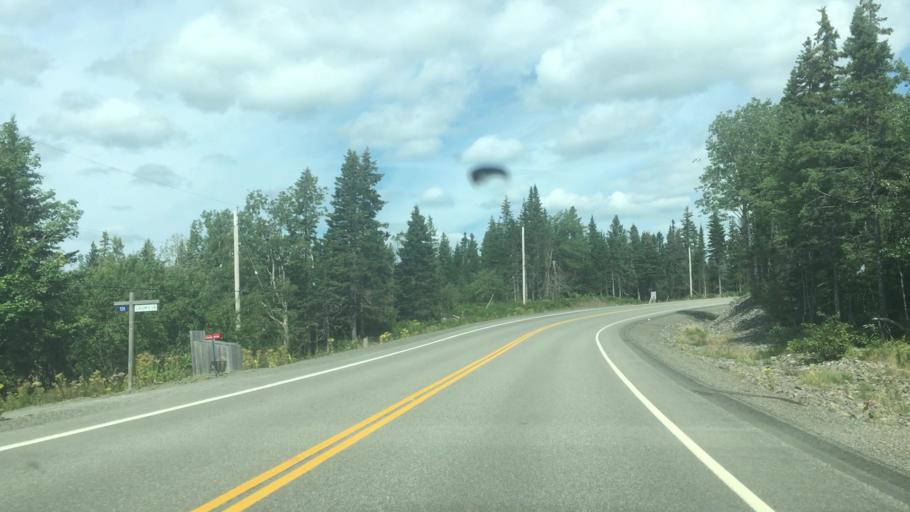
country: CA
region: Nova Scotia
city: Sydney Mines
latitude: 46.3258
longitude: -60.6063
